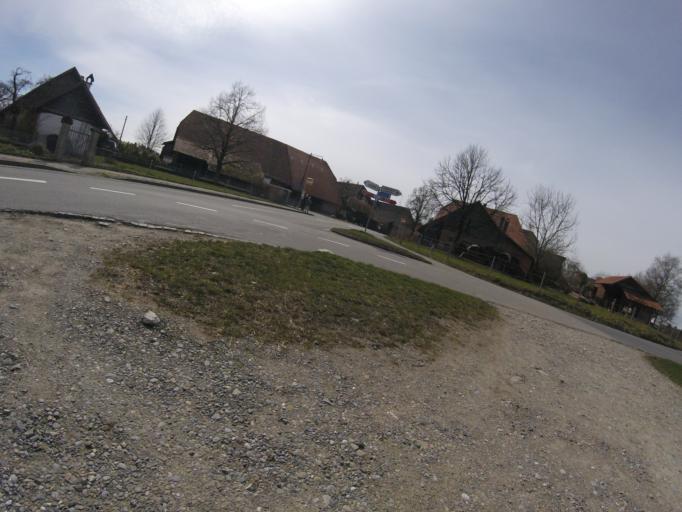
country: CH
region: Bern
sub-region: Bern-Mittelland District
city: Laupen
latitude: 46.9118
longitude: 7.2280
